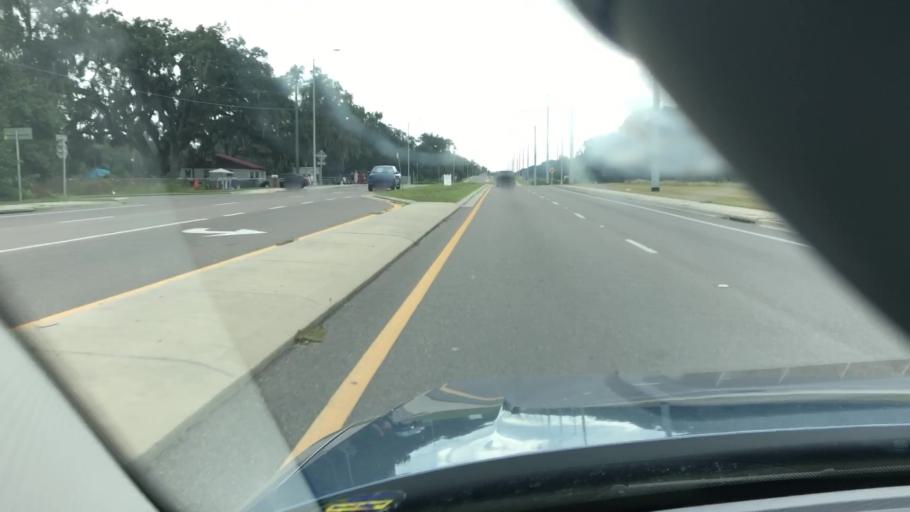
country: US
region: Florida
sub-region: Polk County
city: Kathleen
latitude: 28.1128
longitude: -82.0205
